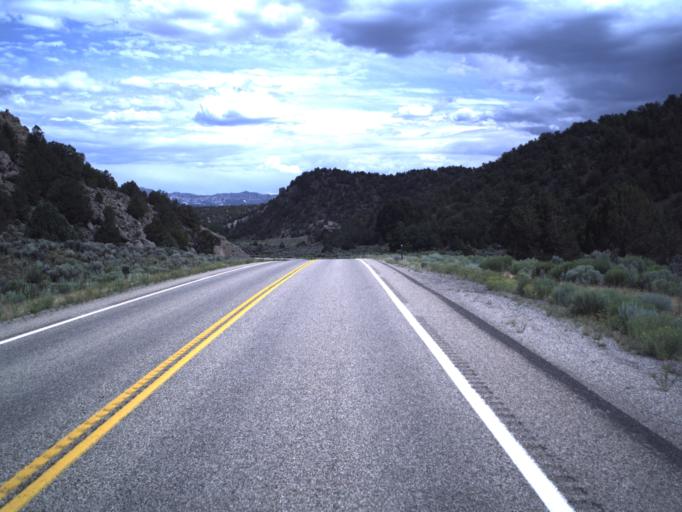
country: US
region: Utah
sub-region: Garfield County
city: Panguitch
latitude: 37.9691
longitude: -112.4780
